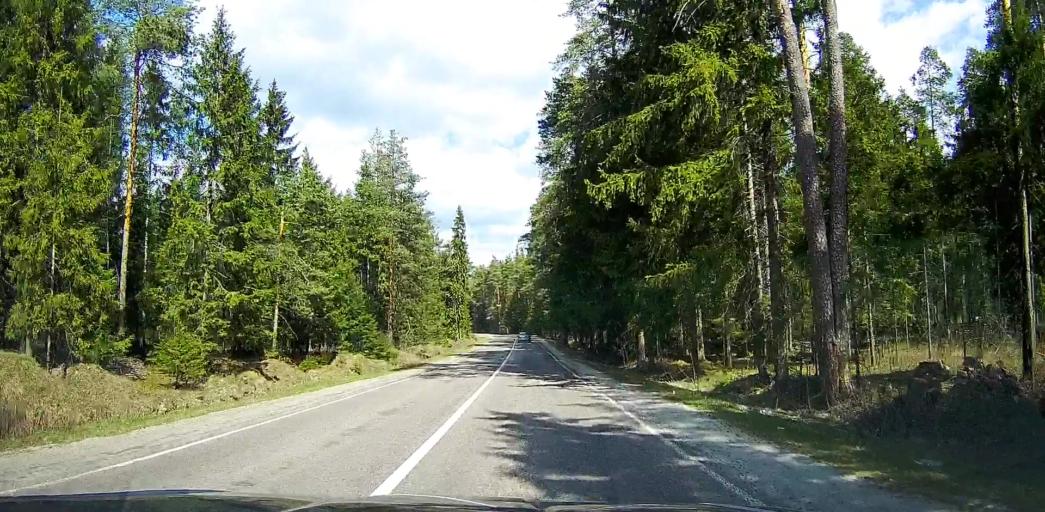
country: RU
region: Moskovskaya
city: Davydovo
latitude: 55.5657
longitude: 38.8188
